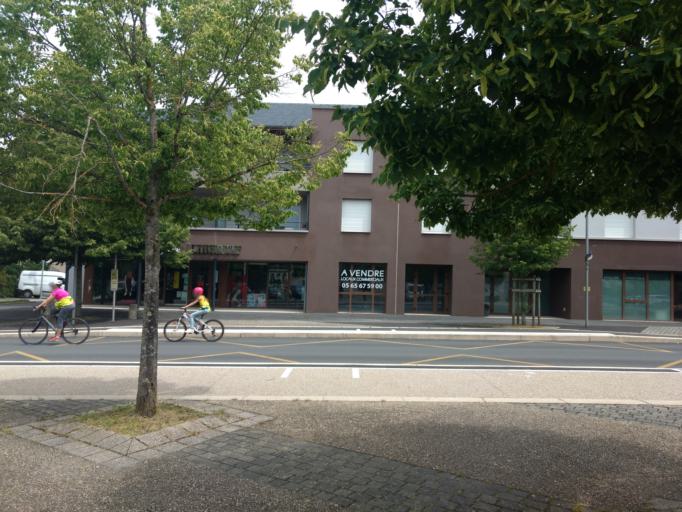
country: FR
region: Midi-Pyrenees
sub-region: Departement de l'Aveyron
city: Olemps
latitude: 44.3414
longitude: 2.5546
